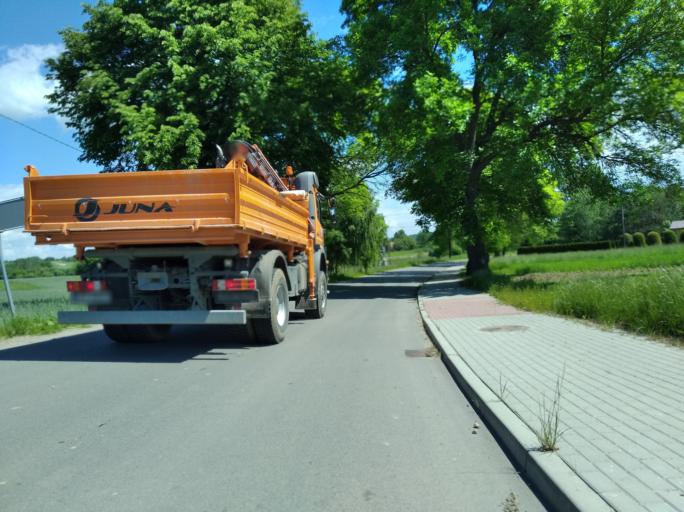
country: PL
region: Subcarpathian Voivodeship
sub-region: Powiat jasielski
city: Tarnowiec
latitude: 49.7633
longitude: 21.6004
